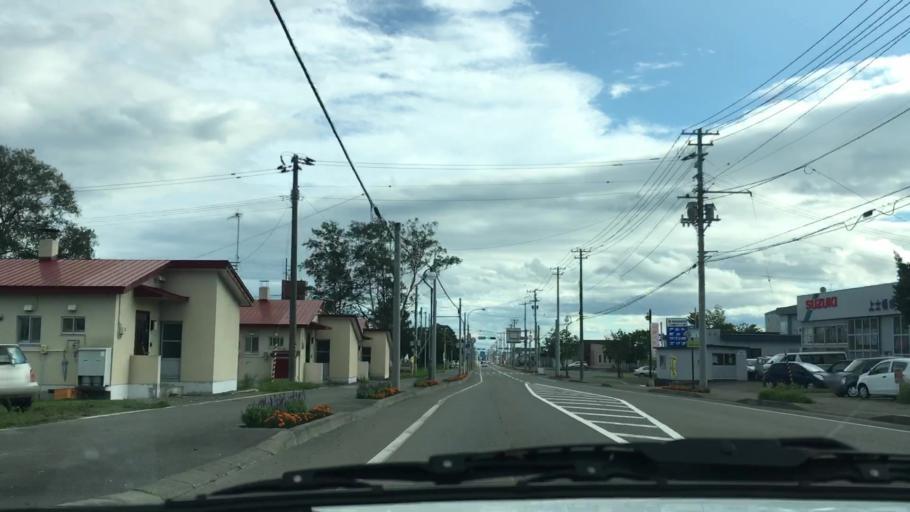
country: JP
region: Hokkaido
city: Otofuke
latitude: 43.2342
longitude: 143.2954
